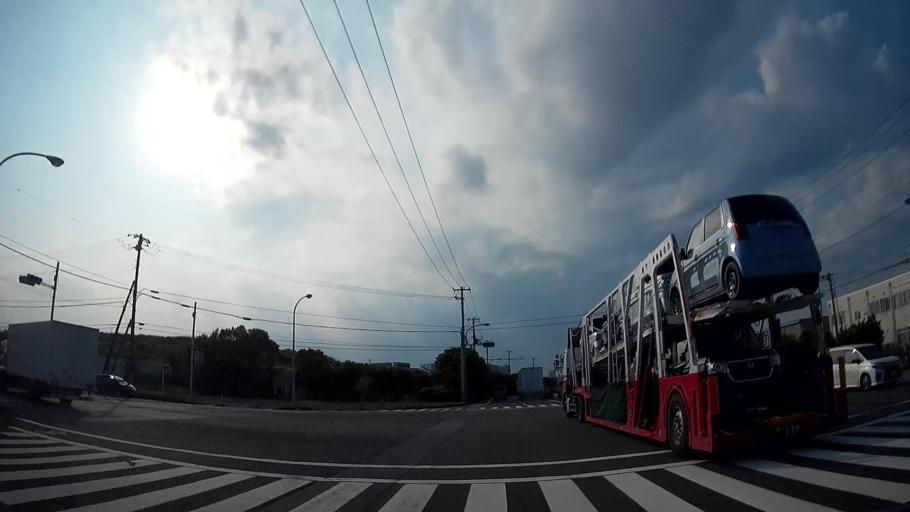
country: JP
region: Chiba
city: Funabashi
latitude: 35.6702
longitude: 140.0029
